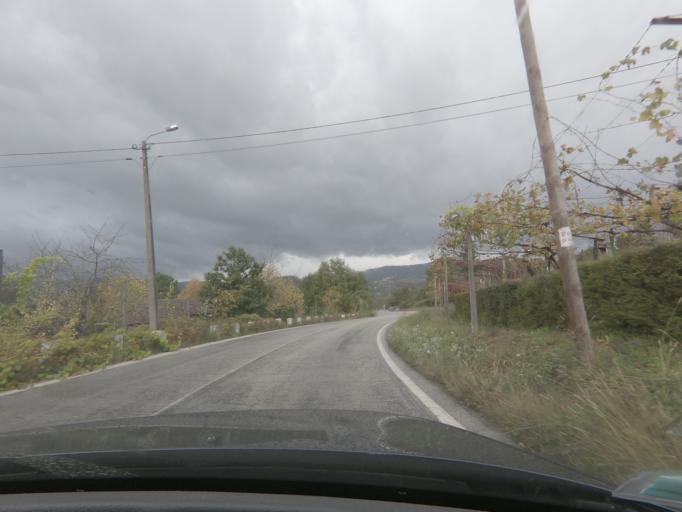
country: PT
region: Vila Real
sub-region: Mondim de Basto
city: Mondim de Basto
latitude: 41.3968
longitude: -7.9605
